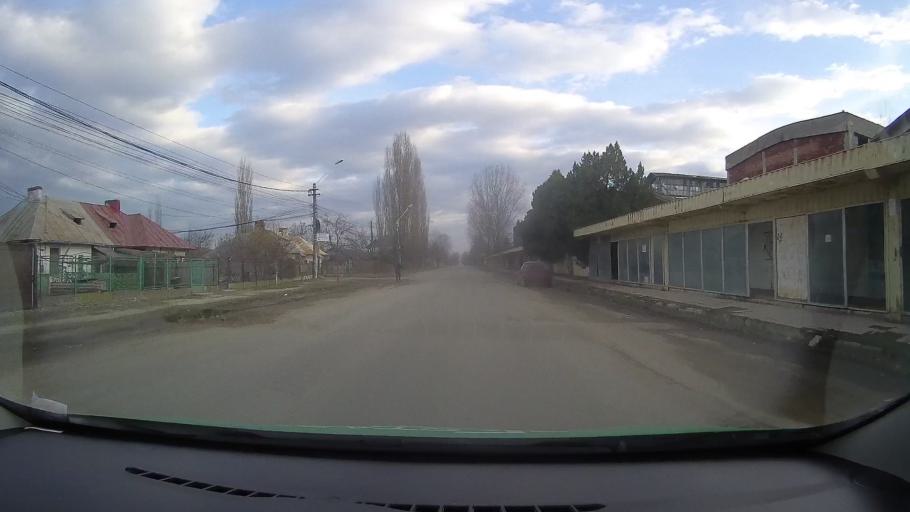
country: RO
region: Dambovita
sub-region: Municipiul Moreni
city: Moreni
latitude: 44.9710
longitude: 25.6509
